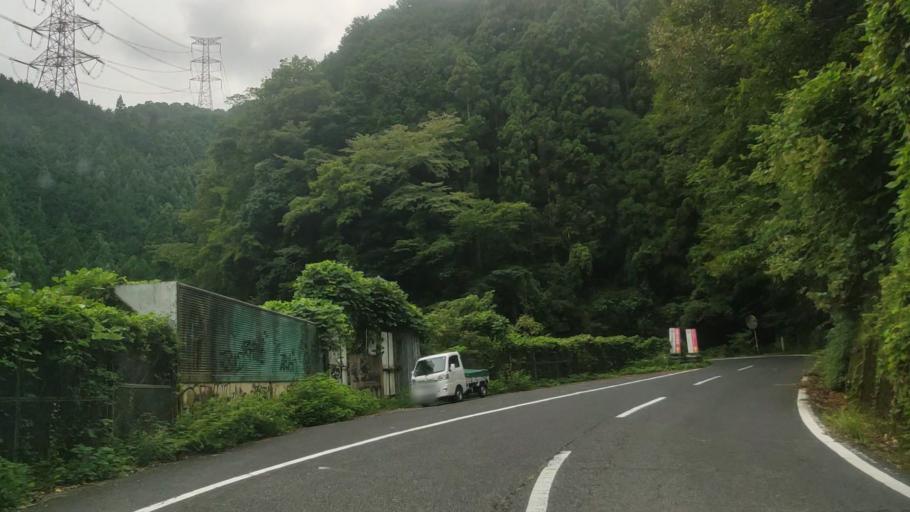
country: JP
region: Wakayama
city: Koya
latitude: 34.2387
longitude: 135.5470
